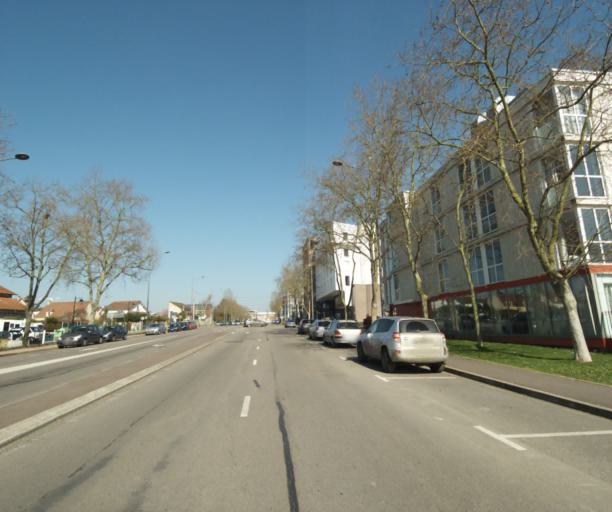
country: FR
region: Ile-de-France
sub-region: Departement du Val-d'Oise
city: Cergy
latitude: 49.0339
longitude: 2.0672
